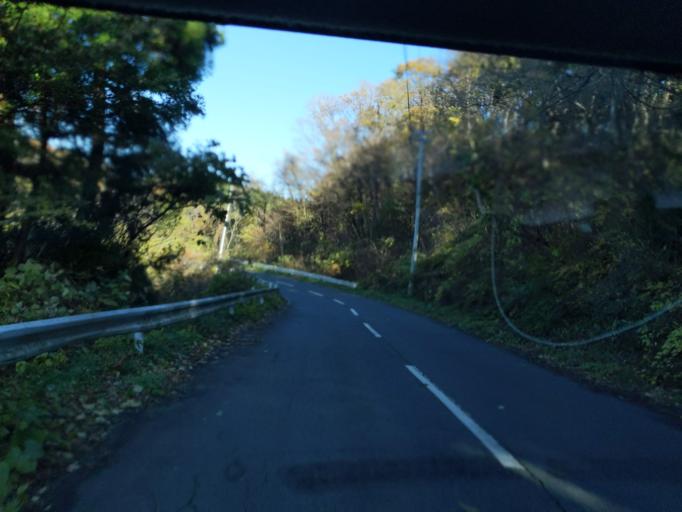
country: JP
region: Iwate
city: Mizusawa
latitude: 39.0825
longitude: 141.1225
